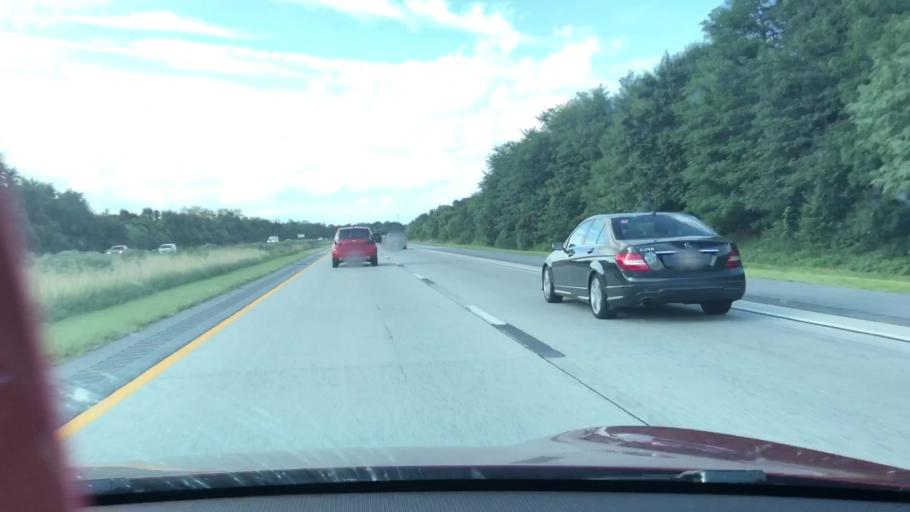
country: US
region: Delaware
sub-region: New Castle County
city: Middletown
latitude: 39.4795
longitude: -75.6499
